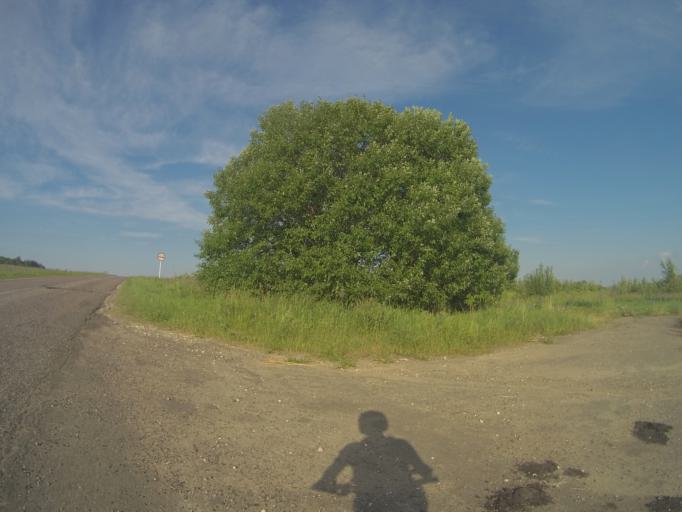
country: RU
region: Vladimir
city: Vladimir
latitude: 56.3115
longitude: 40.2347
